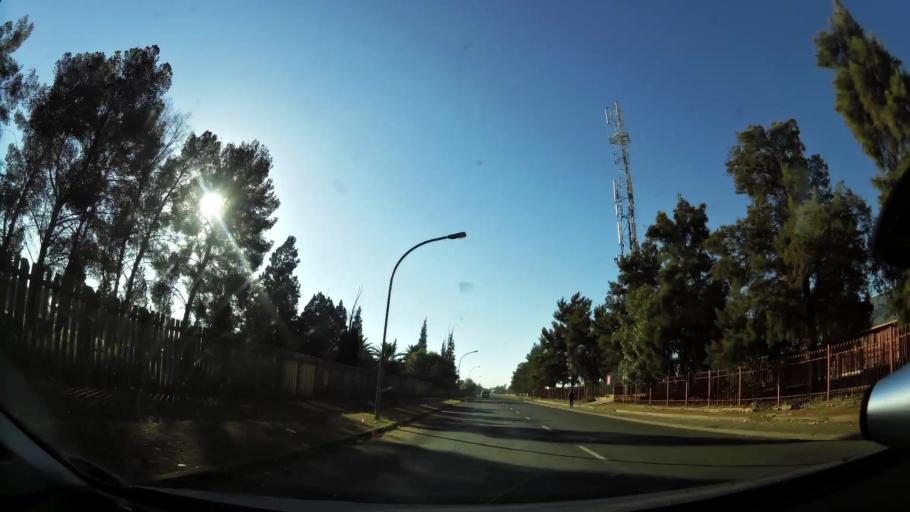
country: ZA
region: Northern Cape
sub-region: Frances Baard District Municipality
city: Kimberley
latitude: -28.7361
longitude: 24.7363
